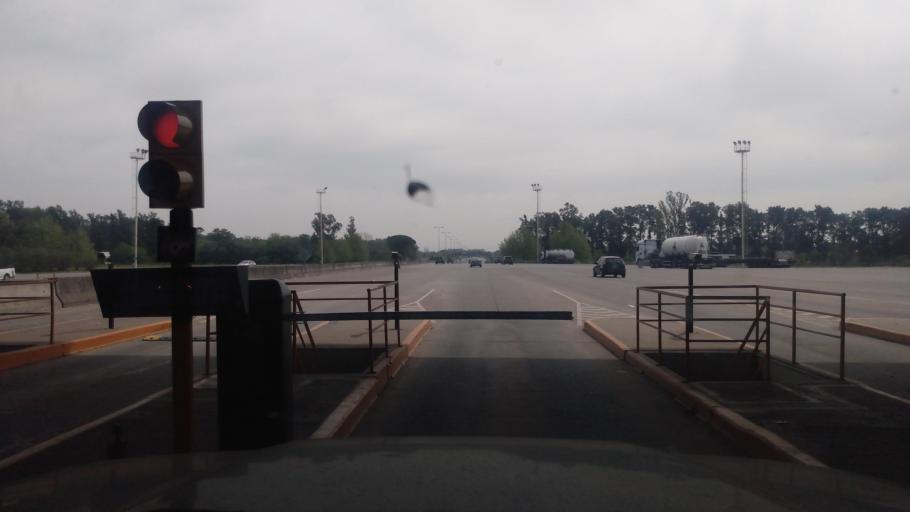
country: AR
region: Buenos Aires
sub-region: Partido de Pilar
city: Pilar
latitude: -34.4031
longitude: -59.0137
